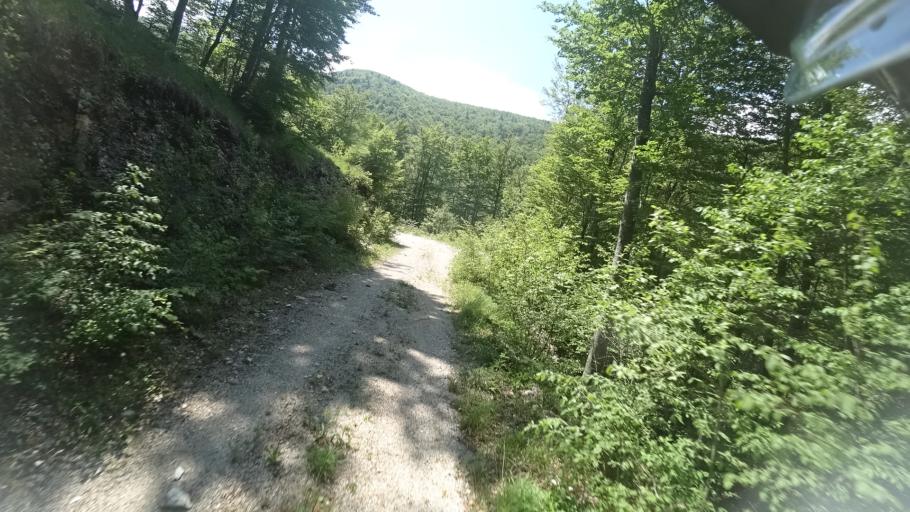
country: BA
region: Federation of Bosnia and Herzegovina
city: Orasac
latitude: 44.5648
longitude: 15.8535
